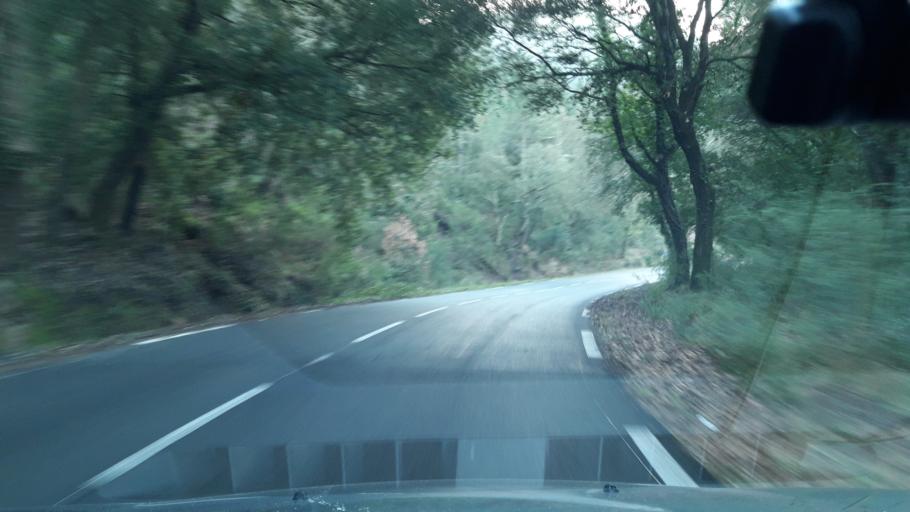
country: FR
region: Provence-Alpes-Cote d'Azur
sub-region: Departement du Var
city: Tanneron
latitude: 43.5112
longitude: 6.8319
